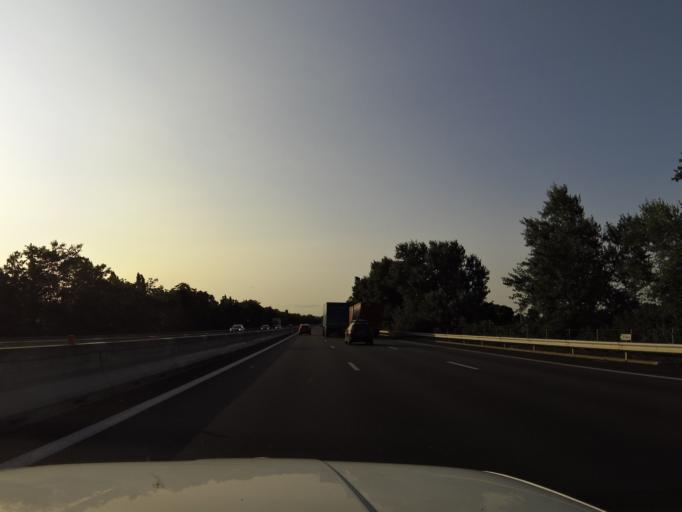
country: FR
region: Rhone-Alpes
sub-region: Departement de la Drome
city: La Roche-de-Glun
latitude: 44.9929
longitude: 4.8800
